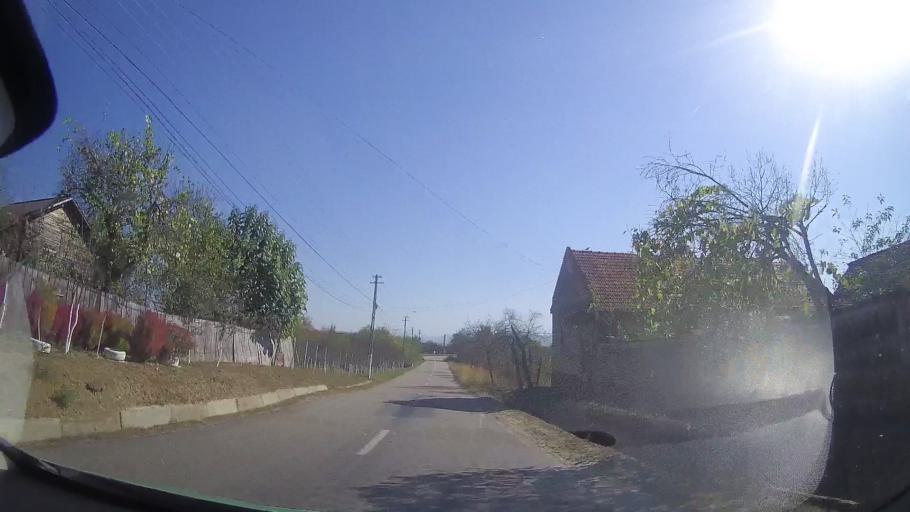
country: RO
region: Timis
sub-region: Comuna Traian Vuia
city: Traian Vuia
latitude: 45.7930
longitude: 22.0235
